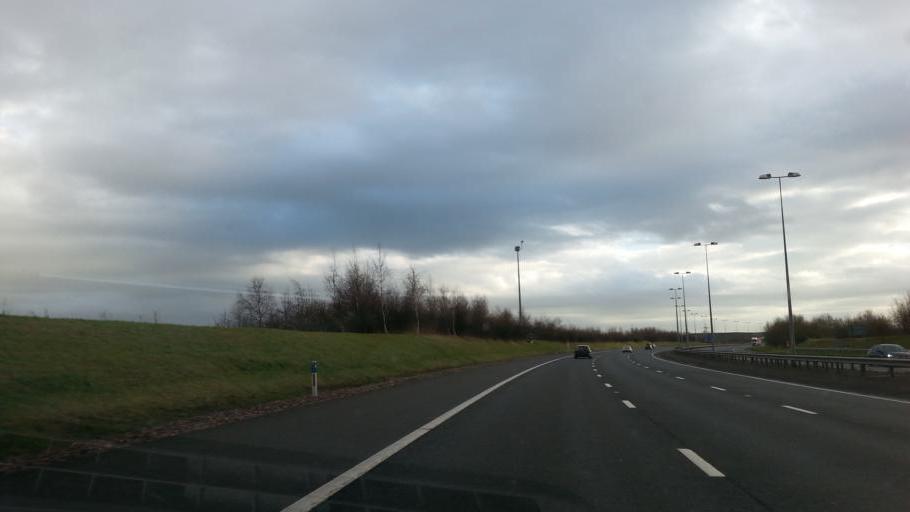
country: GB
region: England
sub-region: Warwickshire
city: Curdworth
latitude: 52.5497
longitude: -1.7330
